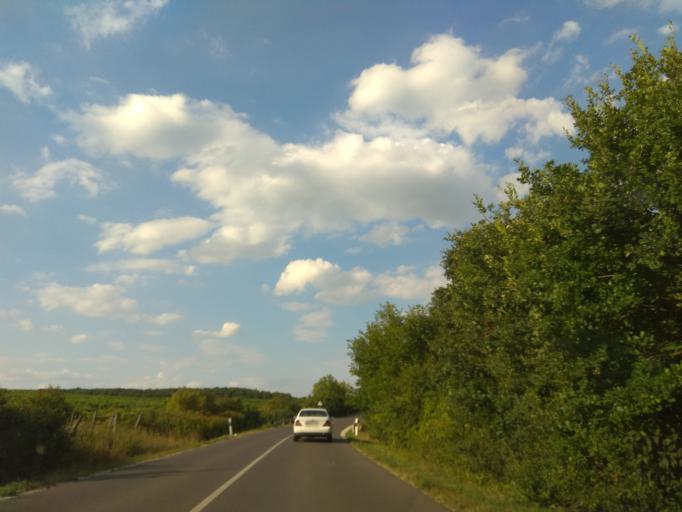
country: HU
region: Borsod-Abauj-Zemplen
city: Harsany
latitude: 47.9855
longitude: 20.7484
